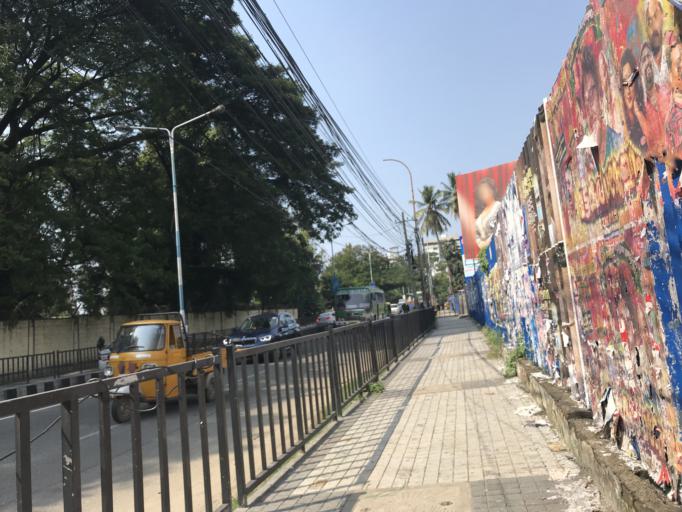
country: IN
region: Kerala
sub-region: Ernakulam
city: Cochin
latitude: 9.9531
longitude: 76.2931
